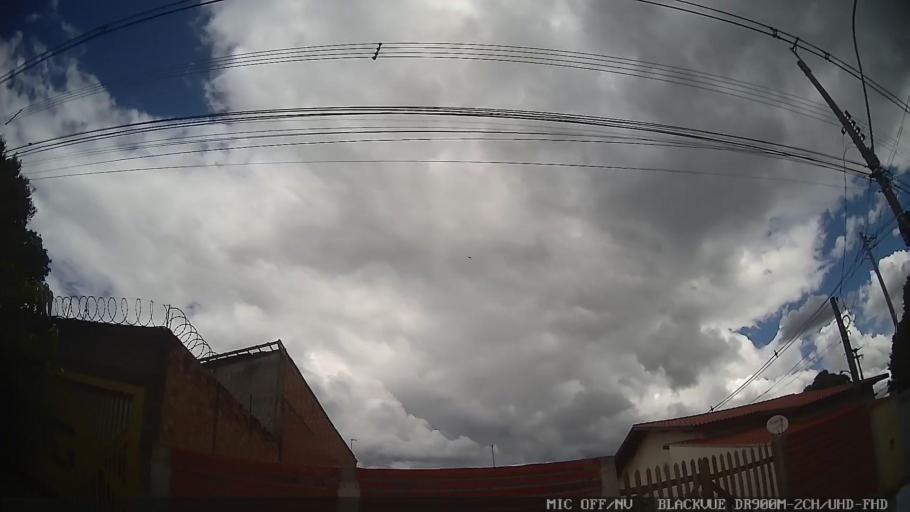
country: BR
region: Sao Paulo
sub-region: Jaguariuna
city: Jaguariuna
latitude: -22.6961
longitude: -47.0040
